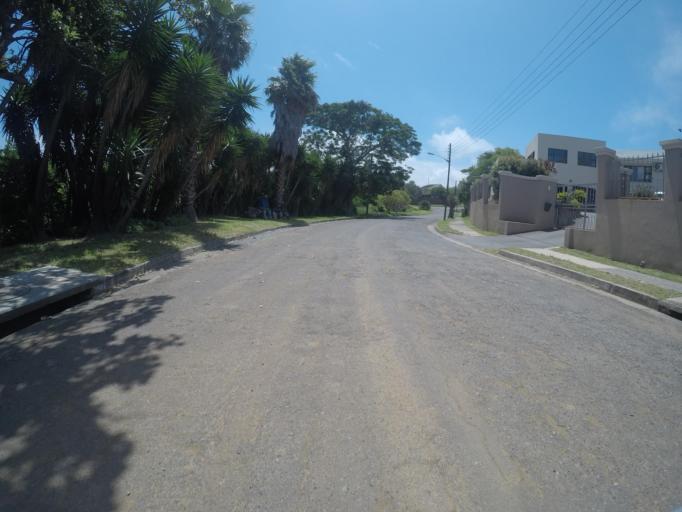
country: ZA
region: Eastern Cape
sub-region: Buffalo City Metropolitan Municipality
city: East London
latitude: -33.0037
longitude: 27.9184
